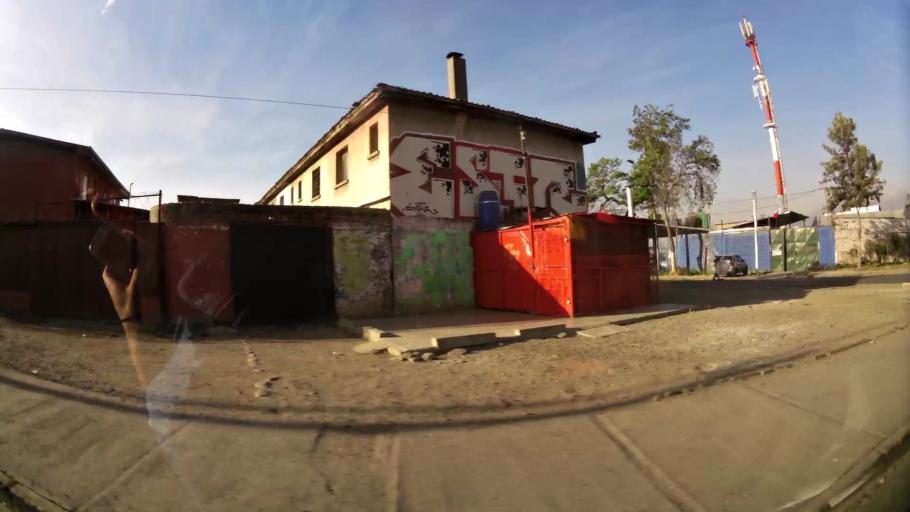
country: CL
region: Santiago Metropolitan
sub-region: Provincia de Santiago
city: Santiago
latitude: -33.4796
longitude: -70.6326
